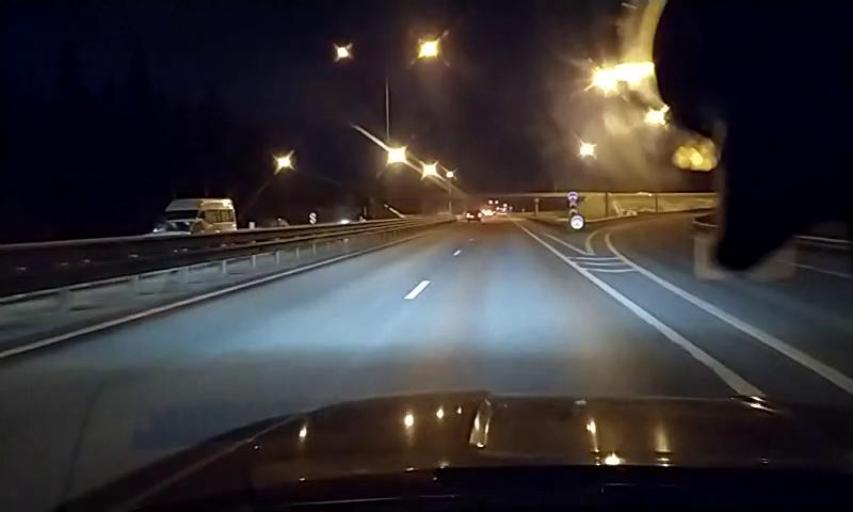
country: RU
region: Leningrad
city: Agalatovo
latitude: 60.2242
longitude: 30.3584
